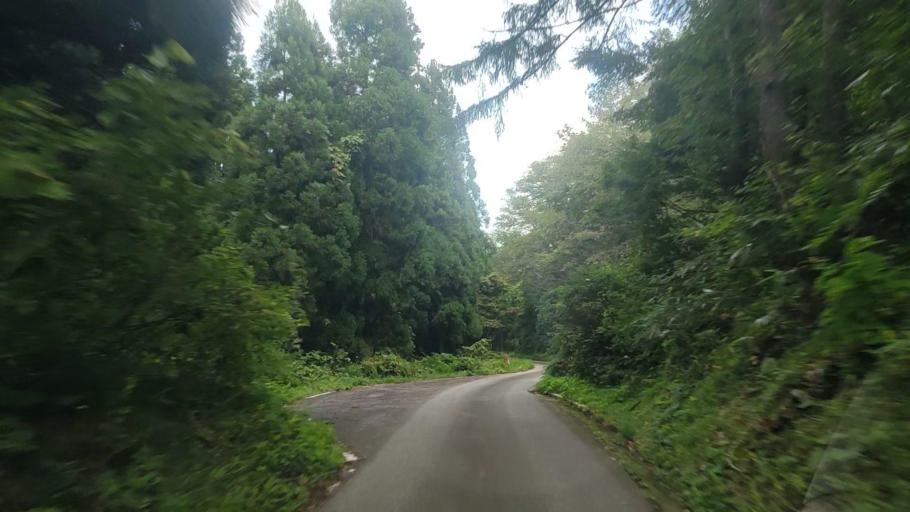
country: JP
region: Toyama
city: Yatsuomachi-higashikumisaka
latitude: 36.4094
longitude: 137.0776
